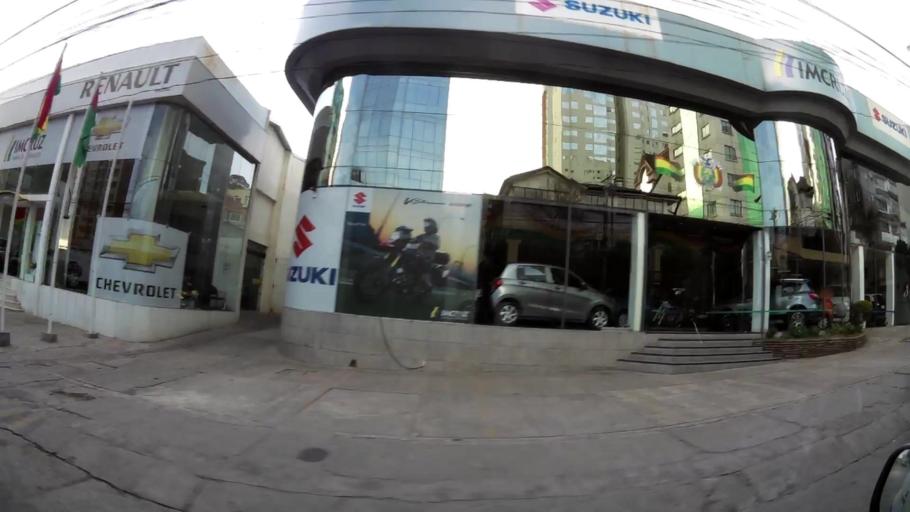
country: BO
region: La Paz
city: La Paz
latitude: -16.5129
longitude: -68.1239
